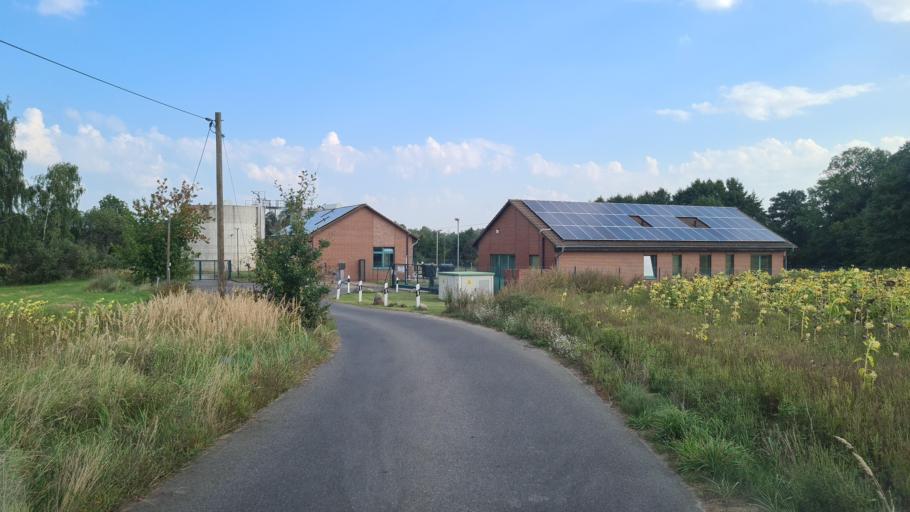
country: DE
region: Brandenburg
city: Drebkau
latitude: 51.6645
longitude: 14.2071
